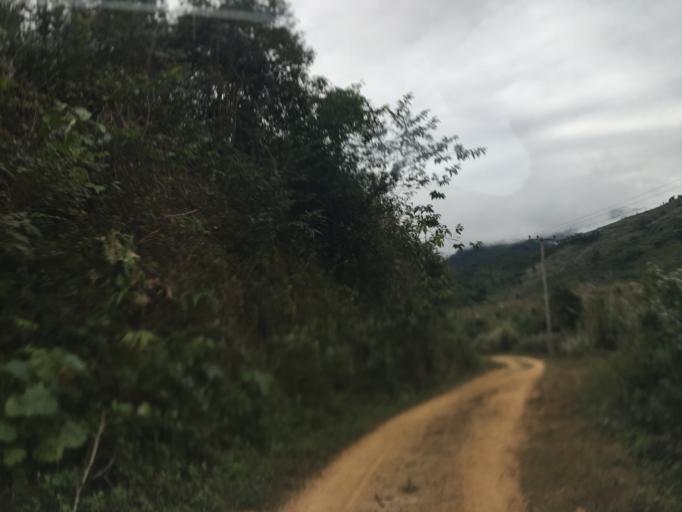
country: LA
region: Houaphan
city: Viengthong
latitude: 19.9408
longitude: 103.2937
